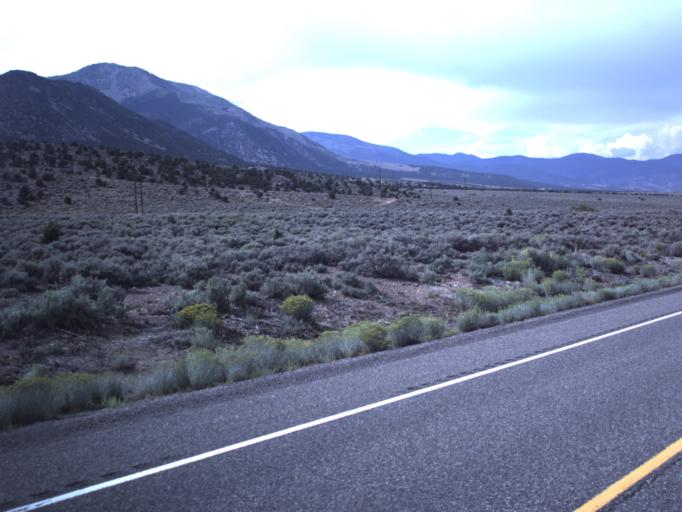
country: US
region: Utah
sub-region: Piute County
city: Junction
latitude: 38.3419
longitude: -112.2180
